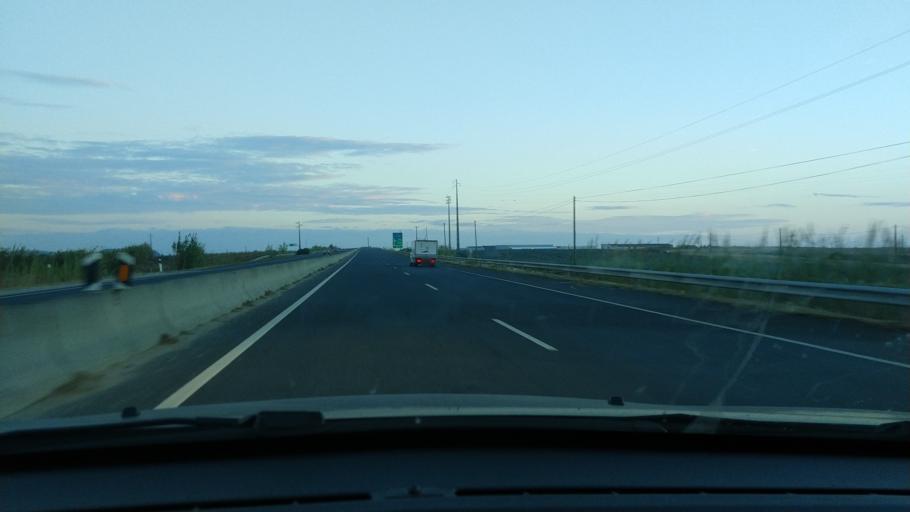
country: PT
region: Leiria
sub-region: Peniche
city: Atouguia da Baleia
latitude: 39.3379
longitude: -9.3372
